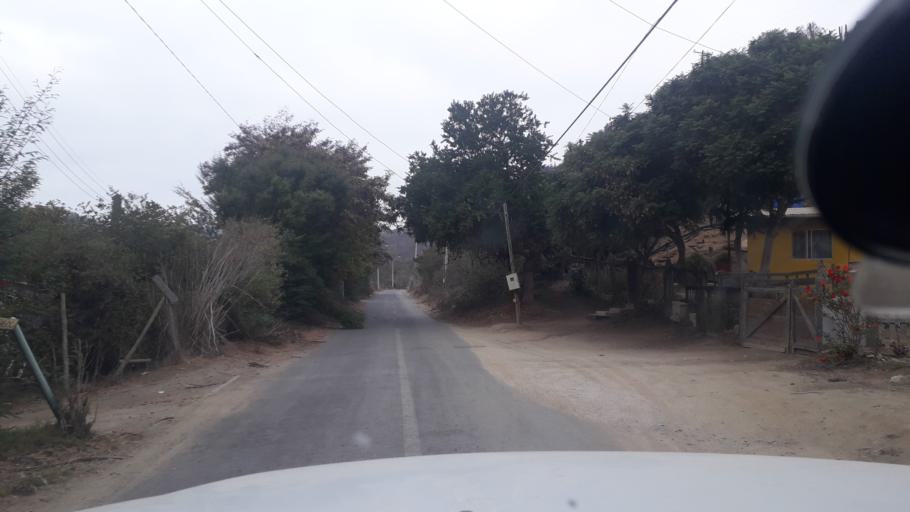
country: CL
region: Valparaiso
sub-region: Provincia de Valparaiso
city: Valparaiso
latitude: -33.1079
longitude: -71.6637
